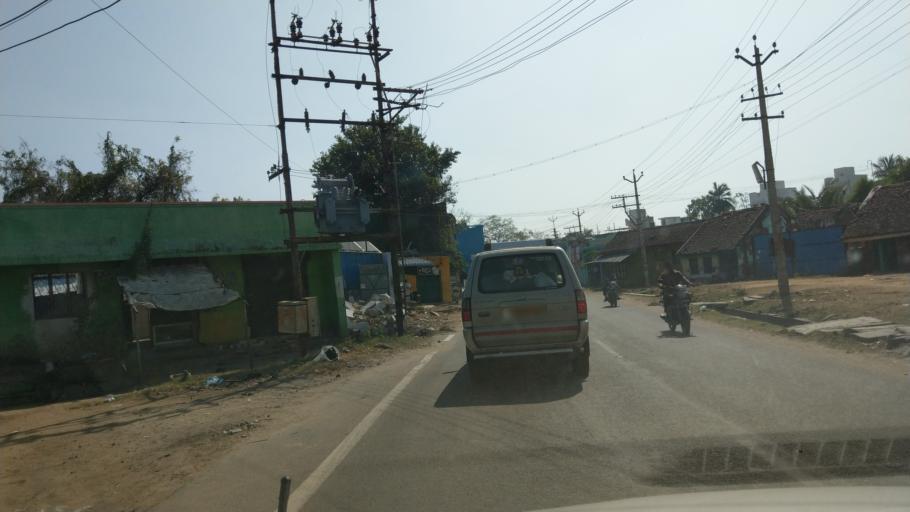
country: IN
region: Tamil Nadu
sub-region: Vellore
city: Arcot
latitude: 12.8983
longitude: 79.3207
